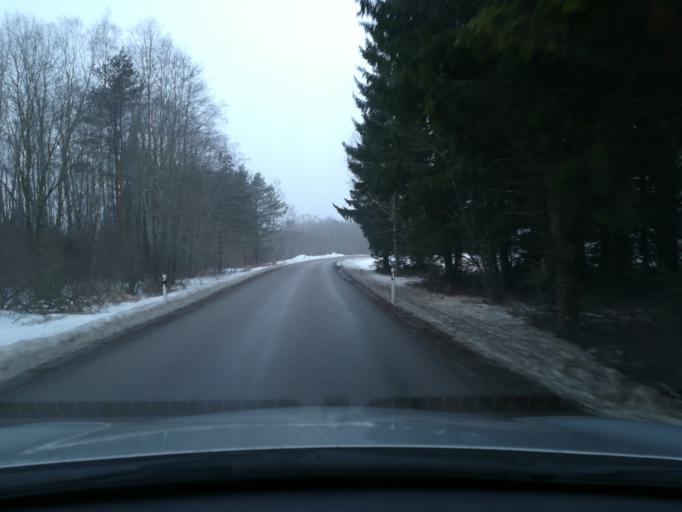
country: EE
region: Harju
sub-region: Rae vald
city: Jueri
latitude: 59.3761
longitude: 24.8993
